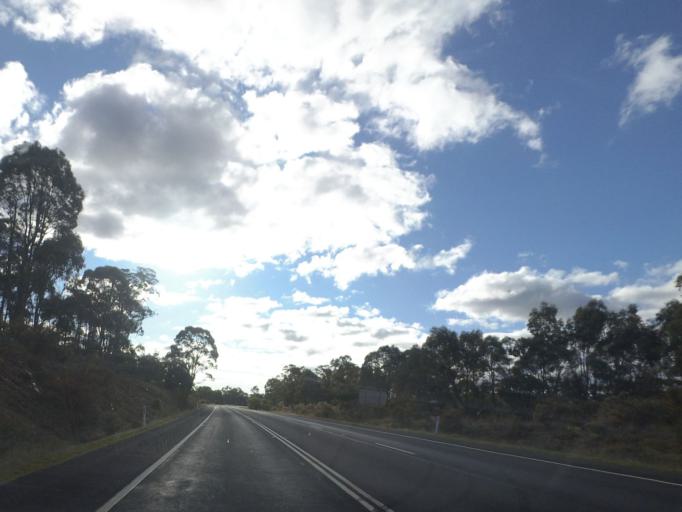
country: AU
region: Victoria
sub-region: Mount Alexander
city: Castlemaine
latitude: -37.1095
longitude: 144.3396
